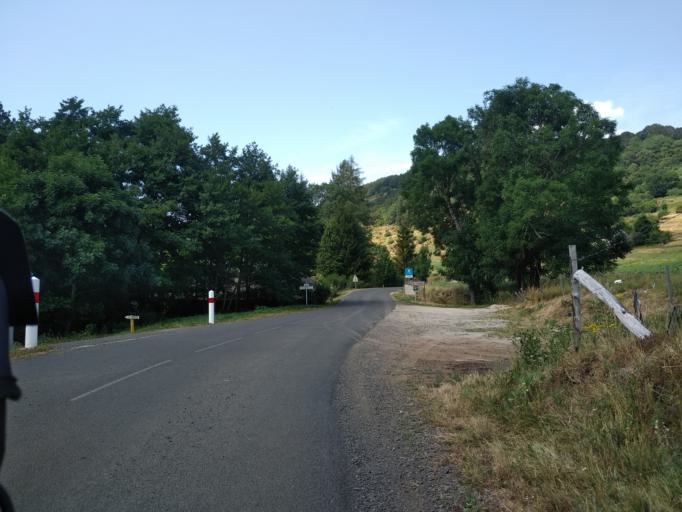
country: FR
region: Auvergne
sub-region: Departement du Cantal
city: Riom-es-Montagnes
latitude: 45.1657
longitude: 2.7104
